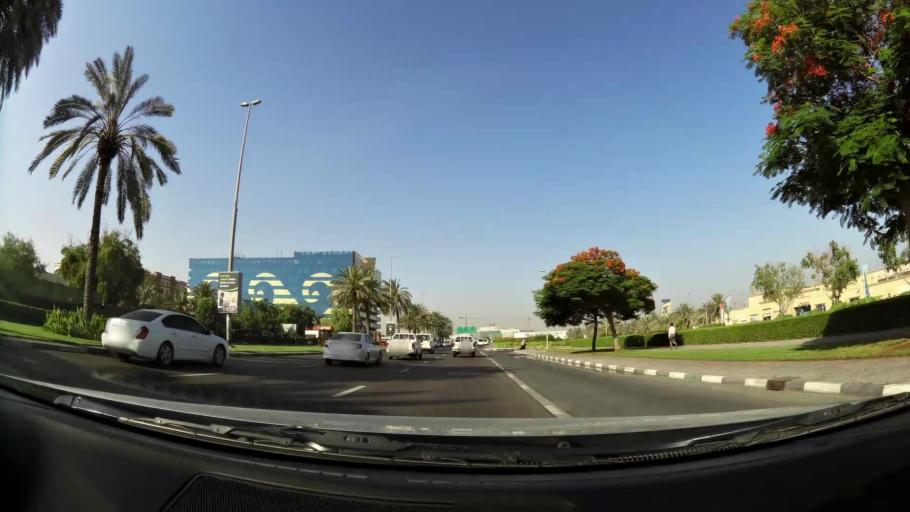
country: AE
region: Ash Shariqah
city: Sharjah
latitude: 25.2534
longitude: 55.2829
